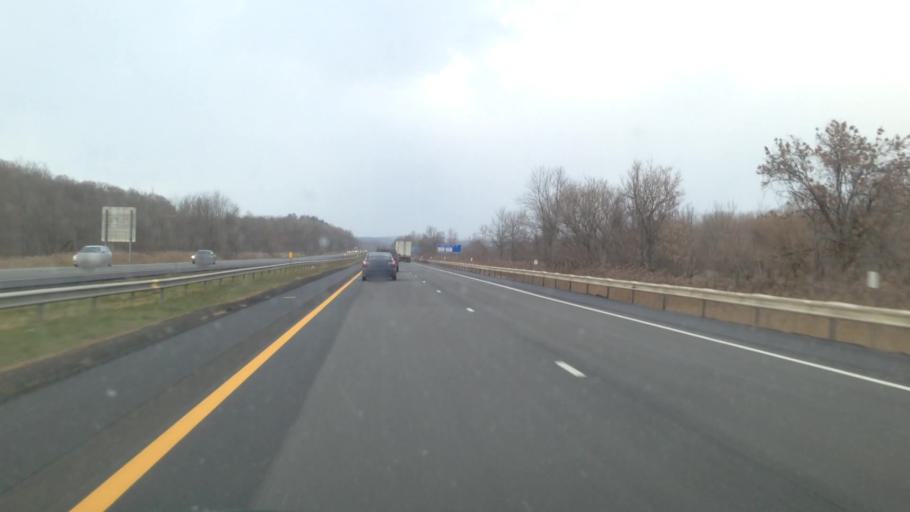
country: US
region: New York
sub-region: Montgomery County
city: Tribes Hill
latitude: 42.9358
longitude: -74.3265
